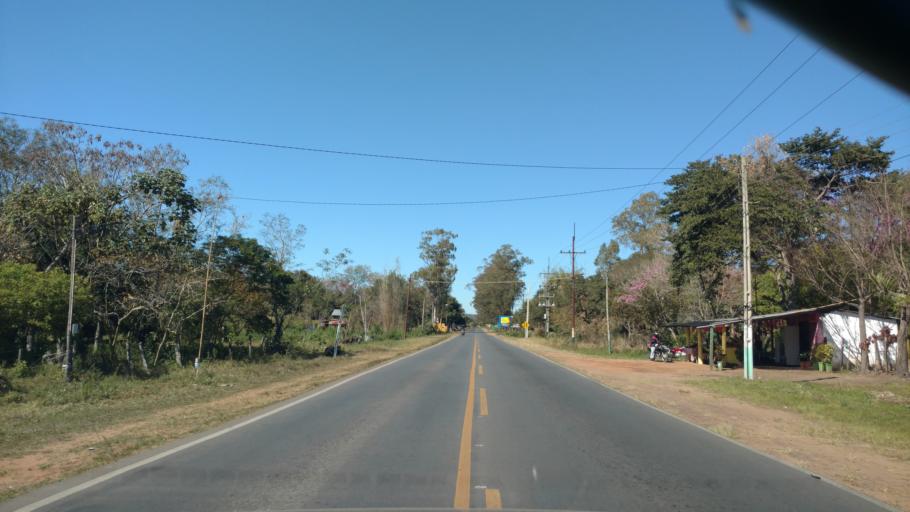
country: PY
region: Central
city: Ypacarai
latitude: -25.4409
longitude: -57.2773
